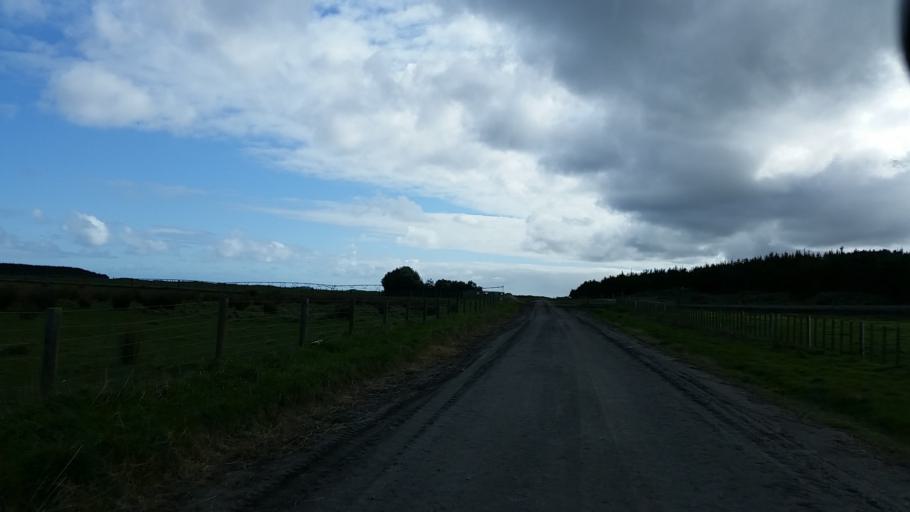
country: NZ
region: Taranaki
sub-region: South Taranaki District
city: Patea
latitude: -39.7990
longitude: 174.5951
